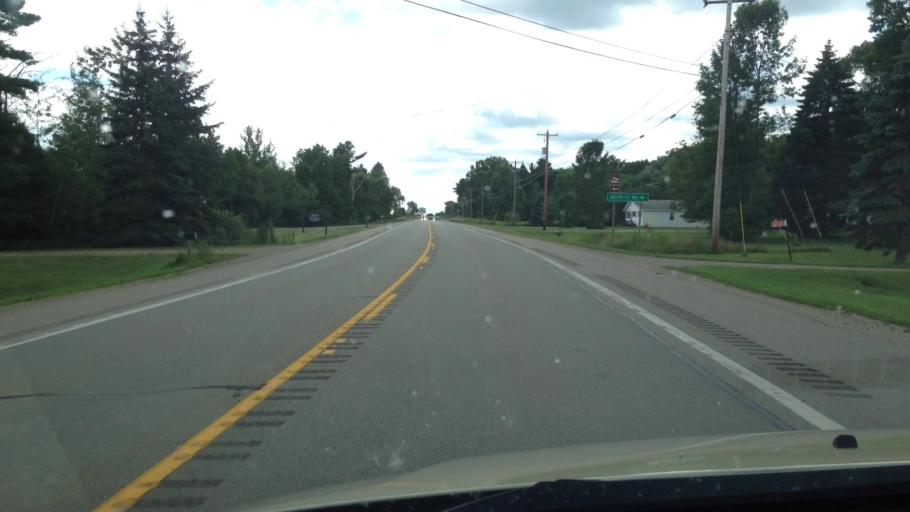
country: US
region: Michigan
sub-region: Menominee County
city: Menominee
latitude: 45.2042
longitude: -87.5364
